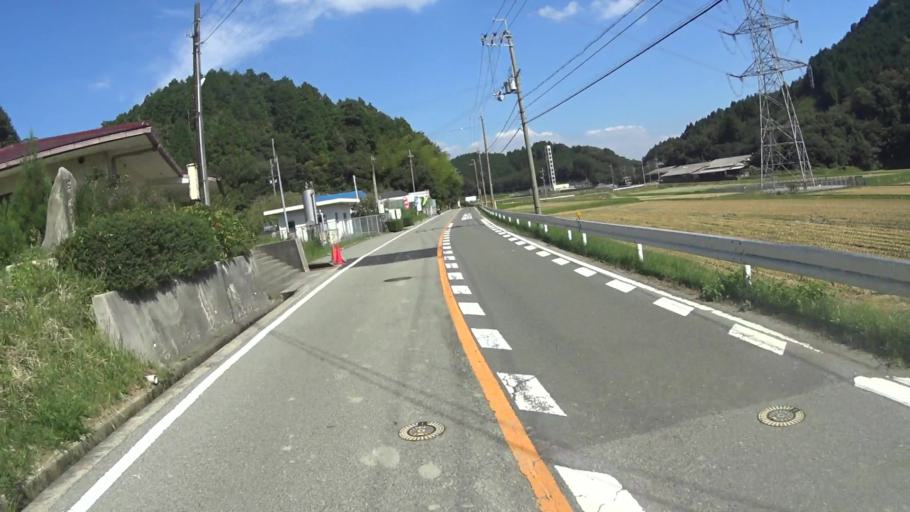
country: JP
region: Kyoto
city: Kameoka
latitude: 34.9731
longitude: 135.5091
